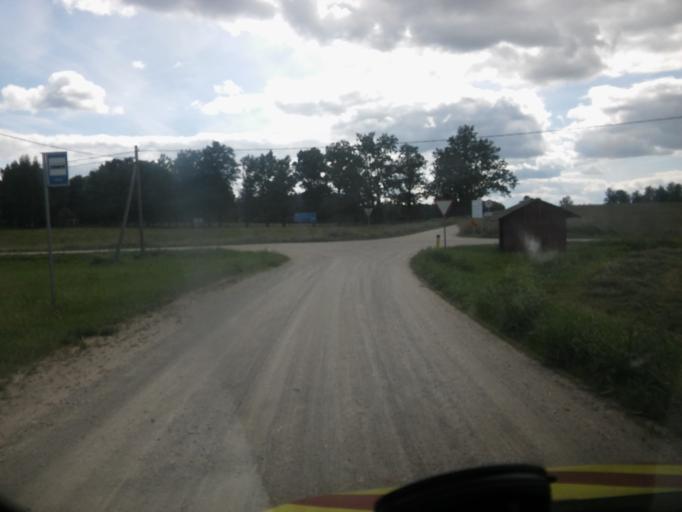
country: EE
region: Viljandimaa
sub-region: Karksi vald
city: Karksi-Nuia
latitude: 58.0888
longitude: 25.4889
